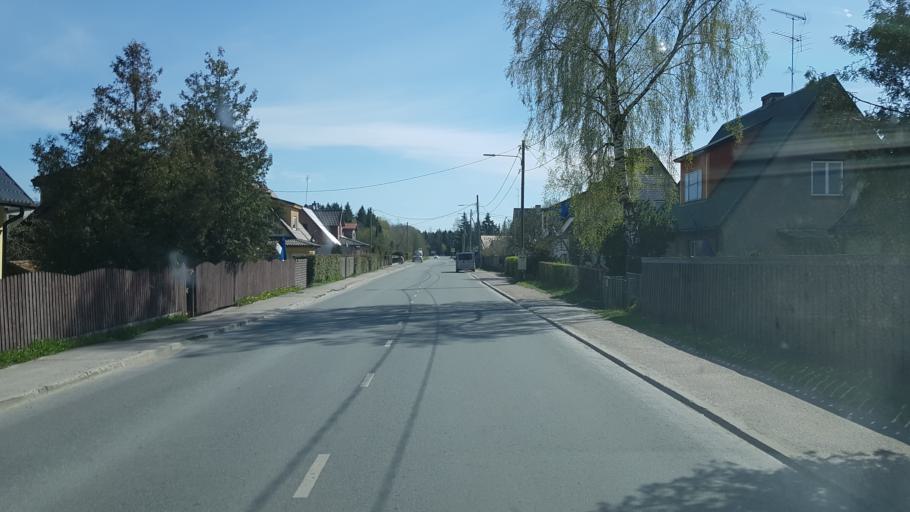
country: EE
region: Harju
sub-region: Keila linn
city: Keila
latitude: 59.3024
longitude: 24.4255
